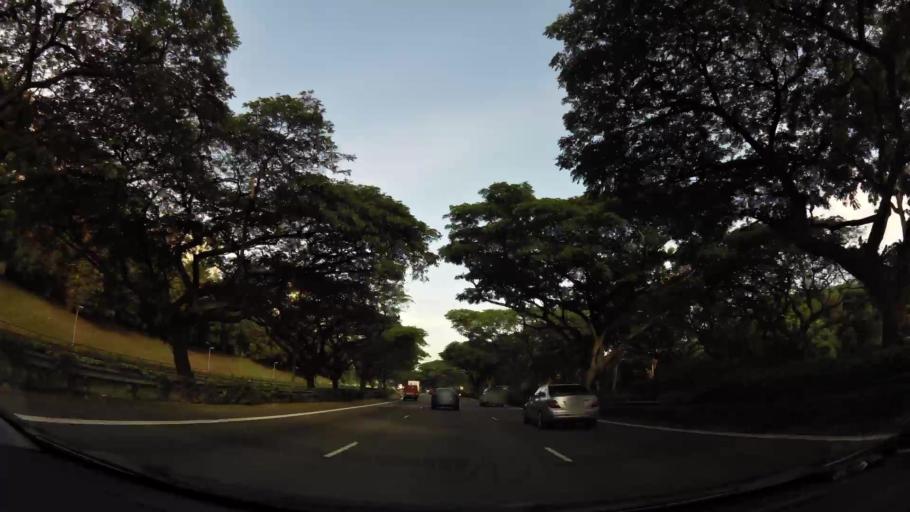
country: MY
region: Johor
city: Johor Bahru
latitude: 1.3511
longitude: 103.7320
